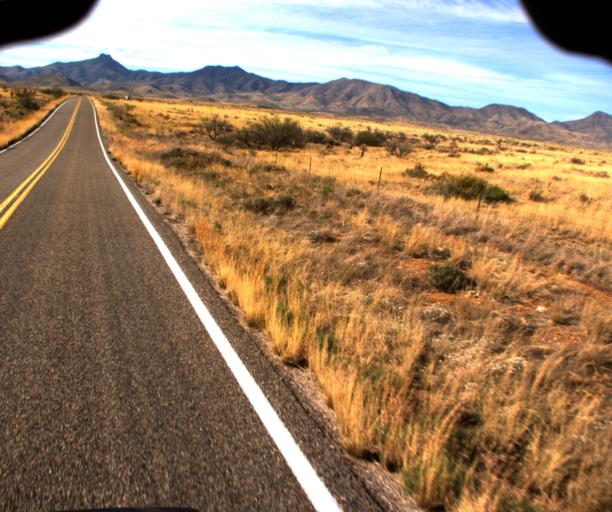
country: US
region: Arizona
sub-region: Cochise County
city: Willcox
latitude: 32.1091
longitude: -109.5482
